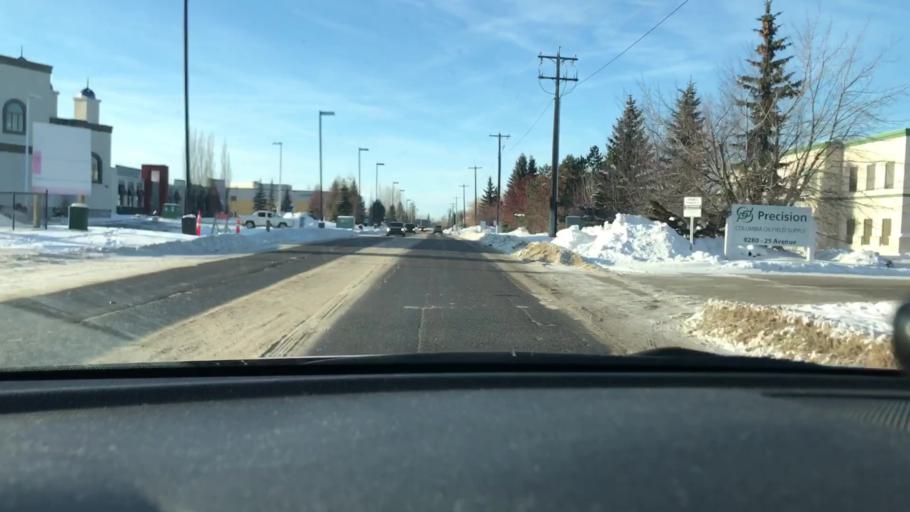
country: CA
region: Alberta
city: Edmonton
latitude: 53.4540
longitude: -113.4718
